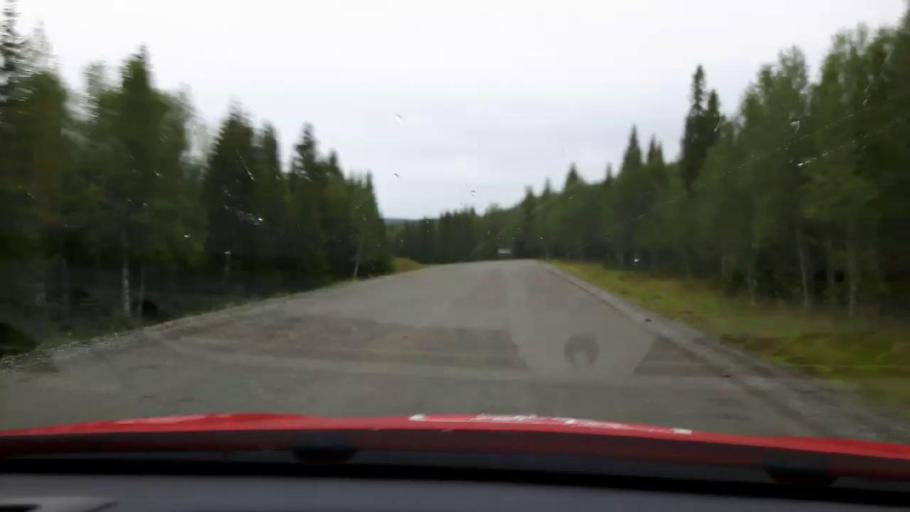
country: SE
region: Jaemtland
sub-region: Are Kommun
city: Are
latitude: 63.4174
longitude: 12.7569
